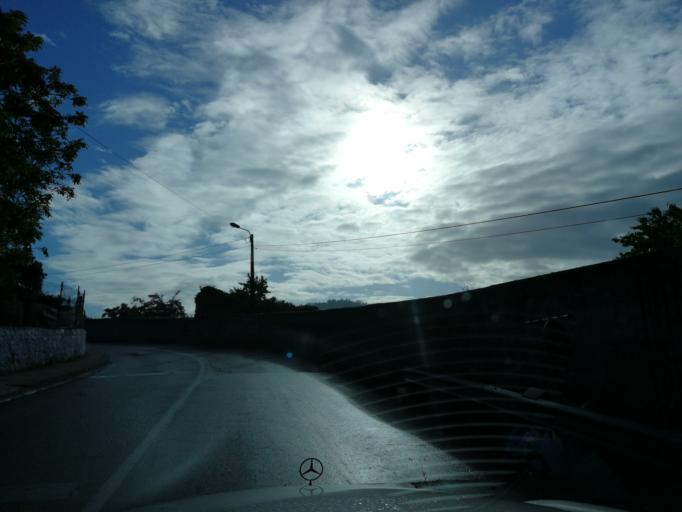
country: PT
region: Braga
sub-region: Braga
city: Braga
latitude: 41.5684
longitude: -8.4323
